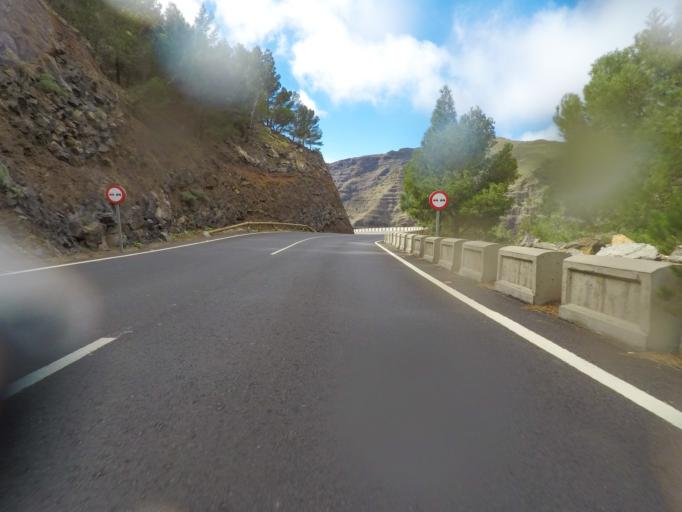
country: ES
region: Canary Islands
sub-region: Provincia de Santa Cruz de Tenerife
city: Vallehermosa
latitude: 28.1184
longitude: -17.3197
